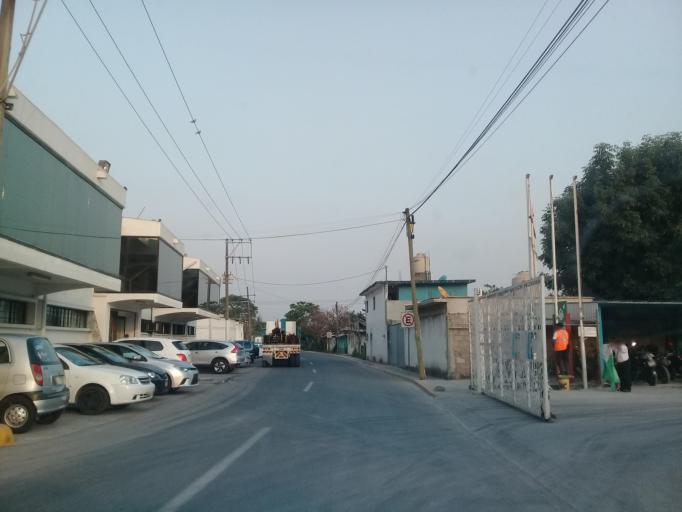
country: MX
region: Veracruz
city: Ixtac Zoquitlan
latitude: 18.8522
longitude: -97.0554
